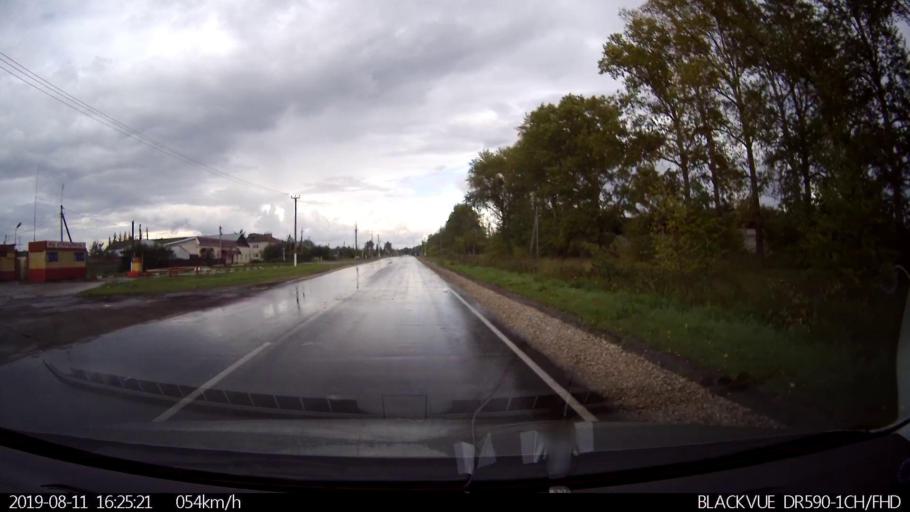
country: RU
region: Ulyanovsk
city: Mayna
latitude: 54.1054
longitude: 47.6035
